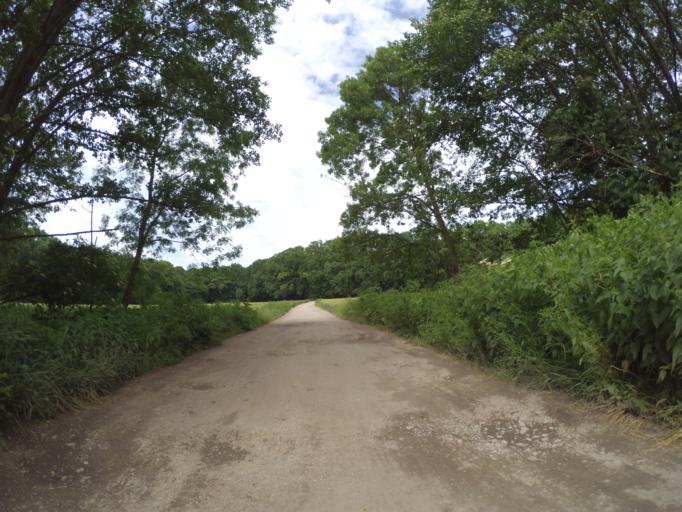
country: CZ
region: Central Bohemia
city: Celakovice
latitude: 50.1773
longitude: 14.7860
